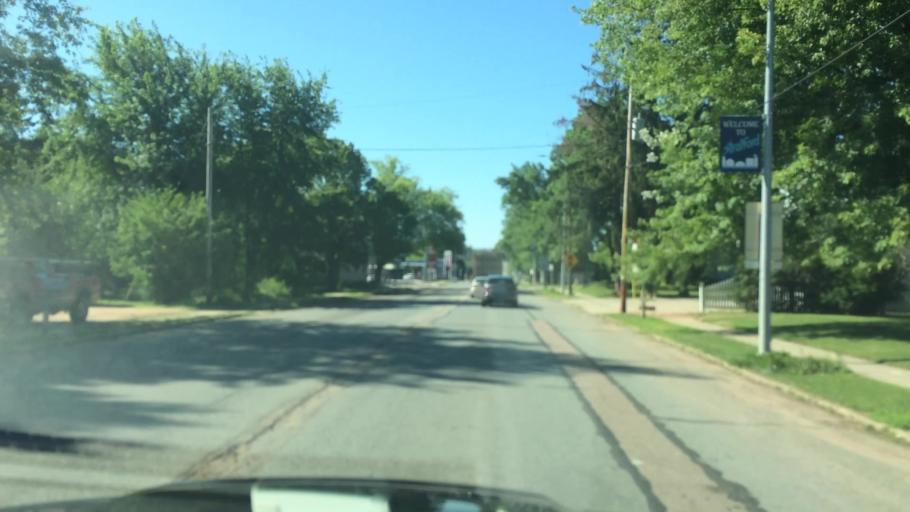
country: US
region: Wisconsin
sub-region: Marathon County
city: Stratford
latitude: 44.8029
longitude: -90.0792
